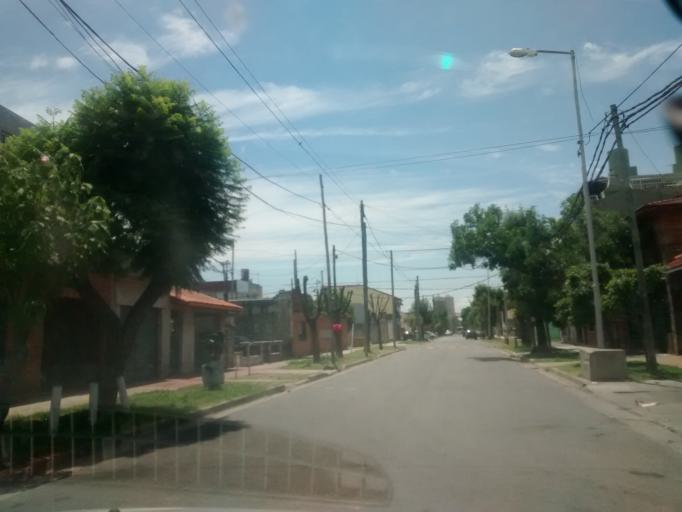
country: AR
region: Buenos Aires
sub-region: Partido de Avellaneda
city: Avellaneda
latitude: -34.6797
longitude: -58.3570
